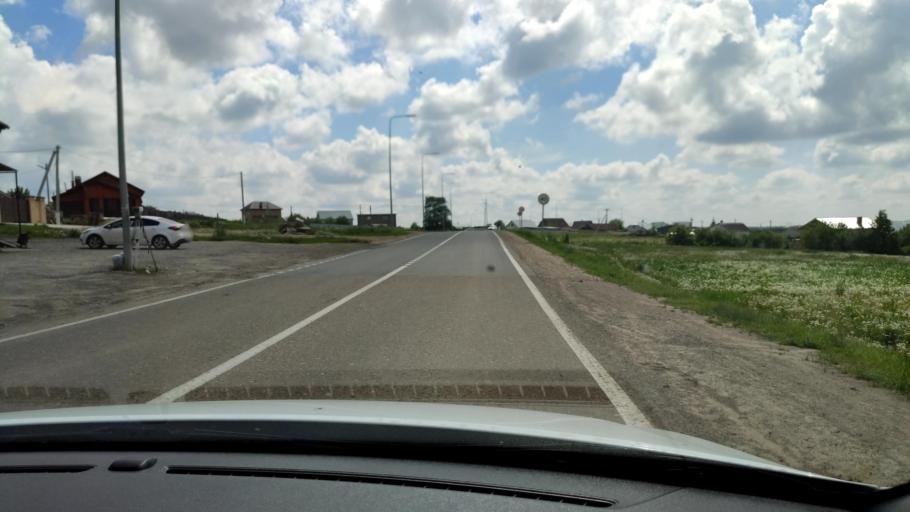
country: RU
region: Tatarstan
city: Vysokaya Gora
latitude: 56.0004
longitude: 49.2984
